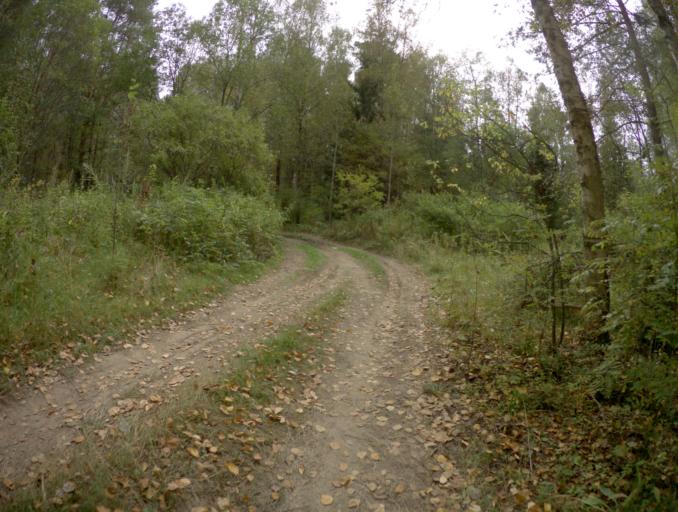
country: RU
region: Vladimir
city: Golovino
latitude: 55.9132
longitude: 40.4319
